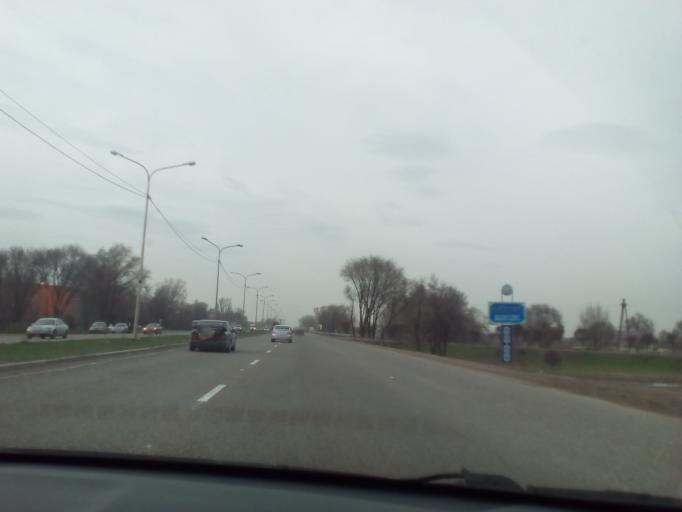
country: KZ
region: Almaty Oblysy
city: Burunday
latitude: 43.2183
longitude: 76.6476
